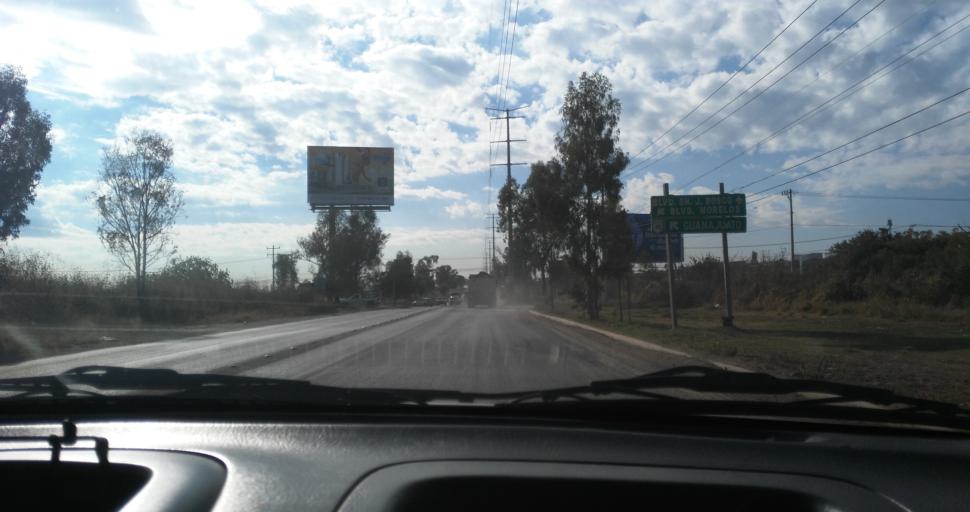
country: MX
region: Guanajuato
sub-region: Leon
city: Fraccionamiento Paseo de las Torres
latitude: 21.1722
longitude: -101.7384
